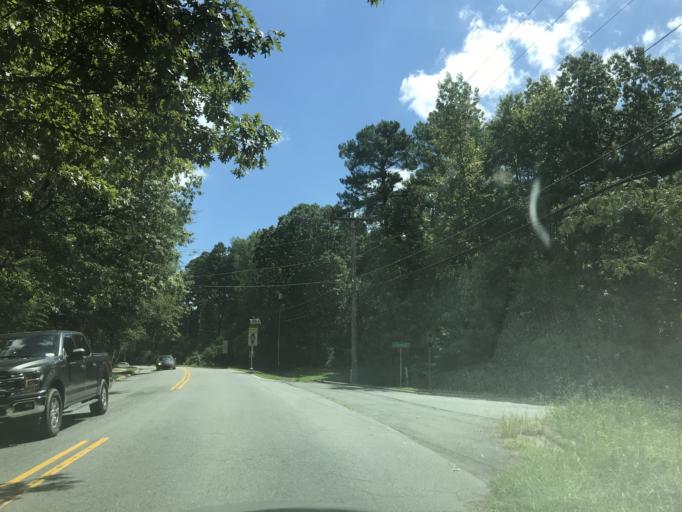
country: US
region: North Carolina
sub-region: Orange County
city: Chapel Hill
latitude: 35.9327
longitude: -79.0185
